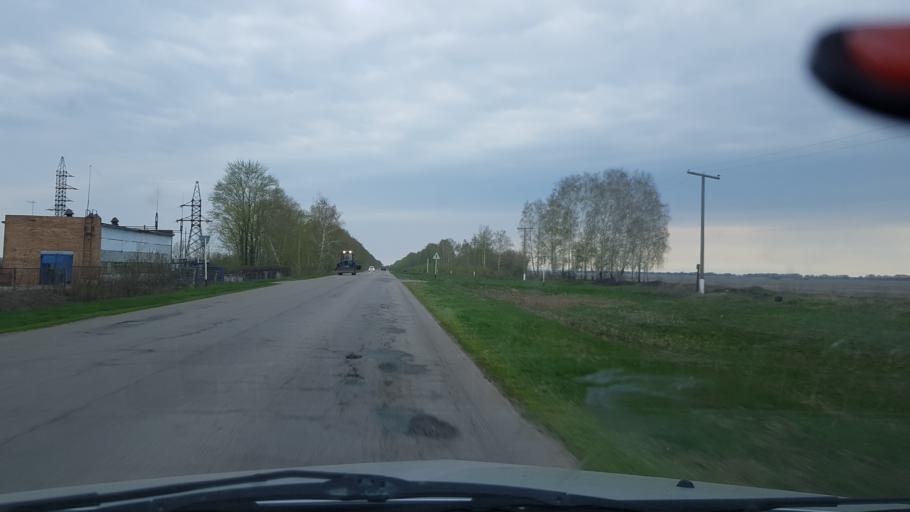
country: RU
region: Samara
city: Podstepki
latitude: 53.6609
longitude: 49.2151
